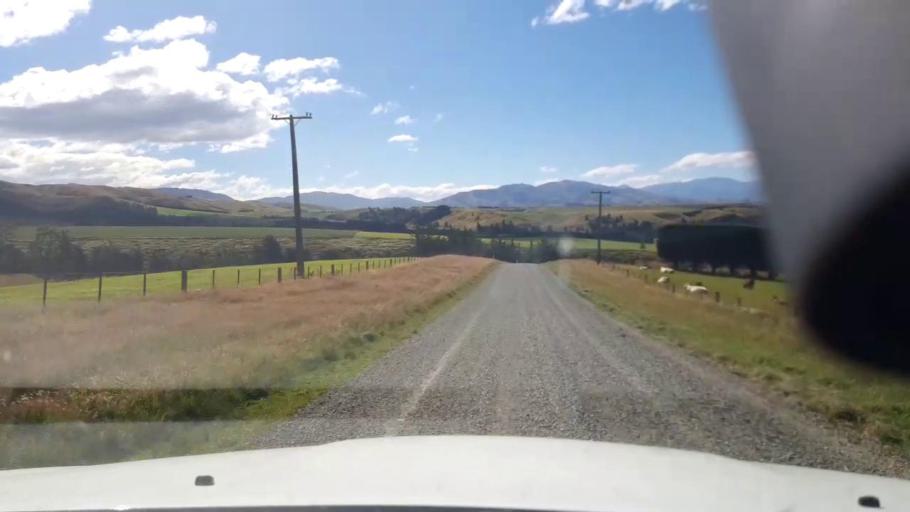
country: NZ
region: Canterbury
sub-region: Timaru District
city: Pleasant Point
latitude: -44.3091
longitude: 170.8745
